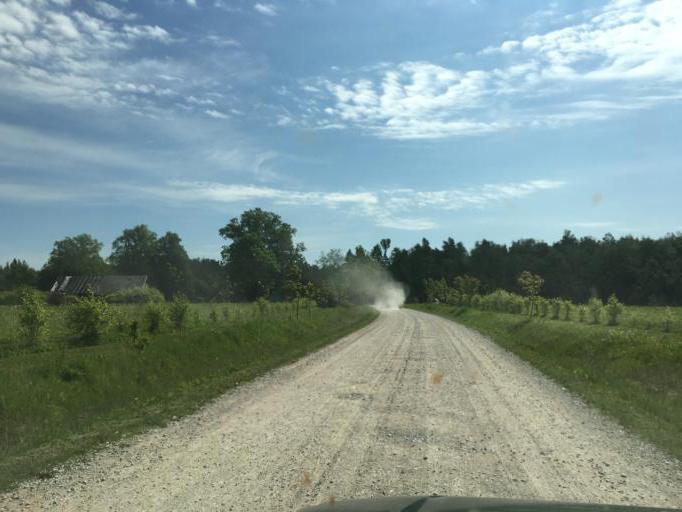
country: LV
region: Talsu Rajons
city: Valdemarpils
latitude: 57.3721
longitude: 22.5228
